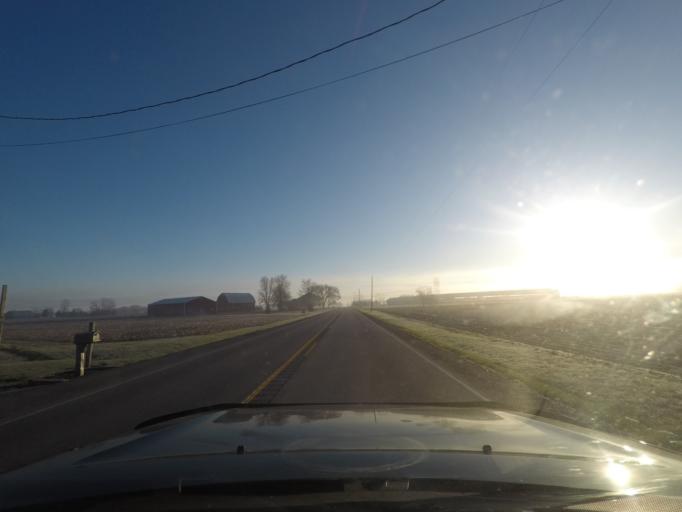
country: US
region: Indiana
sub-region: Elkhart County
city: Wakarusa
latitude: 41.5177
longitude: -85.9748
